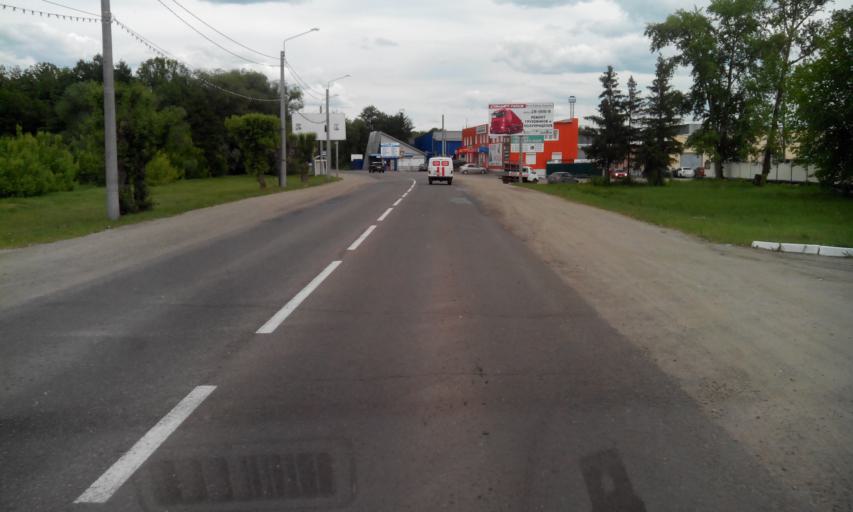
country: RU
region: Penza
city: Penza
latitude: 53.2103
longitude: 45.0735
